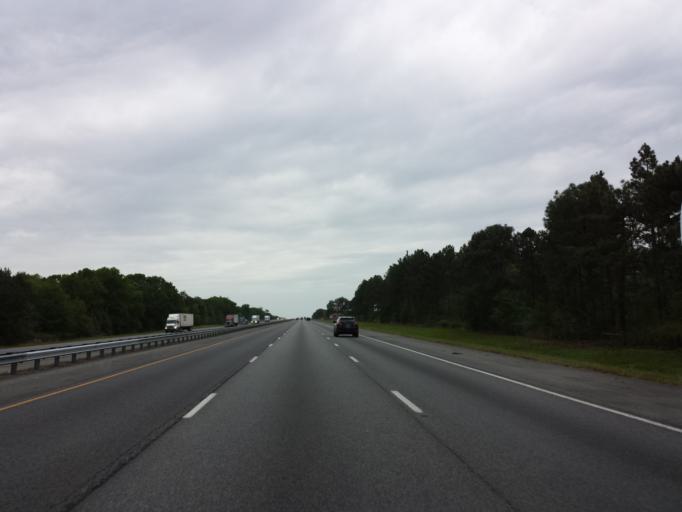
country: US
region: Georgia
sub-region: Crisp County
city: Cordele
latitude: 31.8629
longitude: -83.7214
